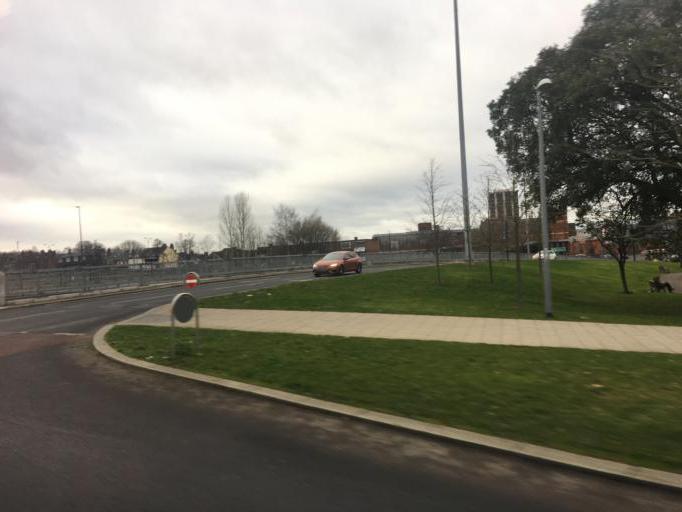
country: GB
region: England
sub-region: Coventry
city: Coventry
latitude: 52.4034
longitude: -1.5143
